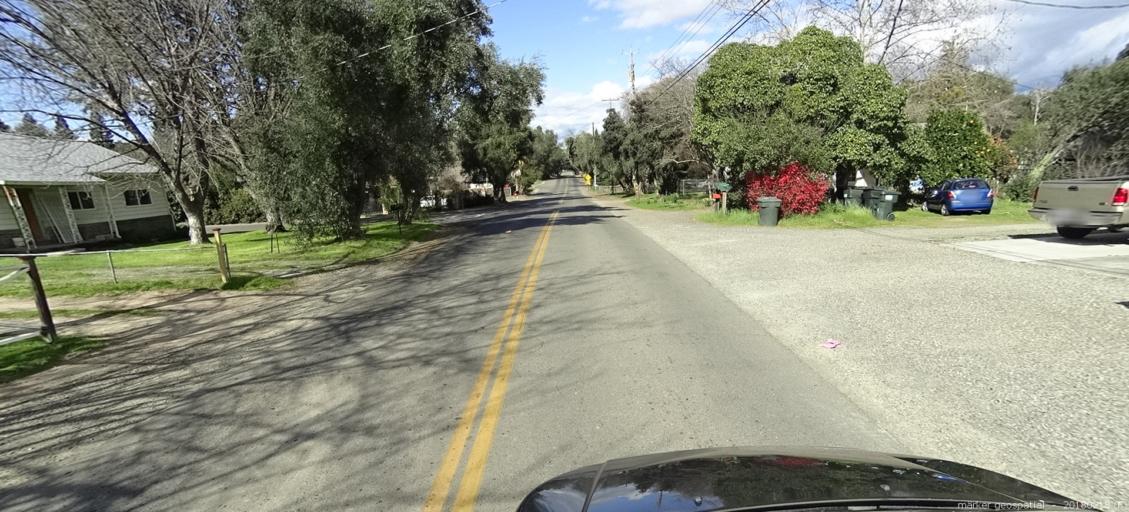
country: US
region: California
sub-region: Sacramento County
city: Orangevale
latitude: 38.6828
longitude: -121.2068
